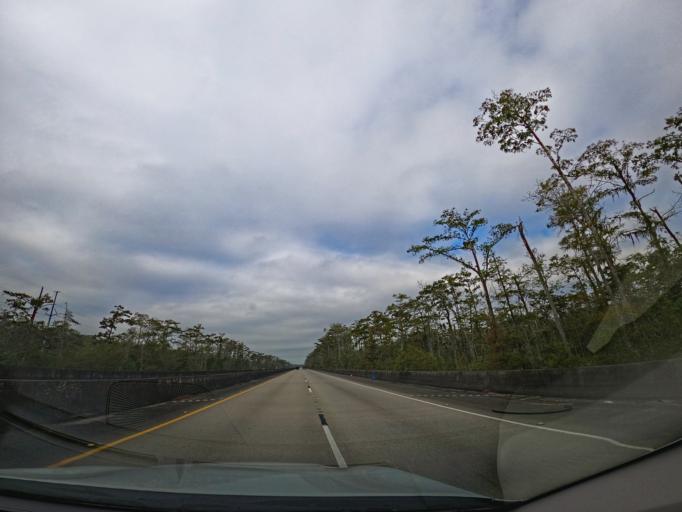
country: US
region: Louisiana
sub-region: Saint Mary Parish
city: Amelia
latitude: 29.6682
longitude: -91.0594
